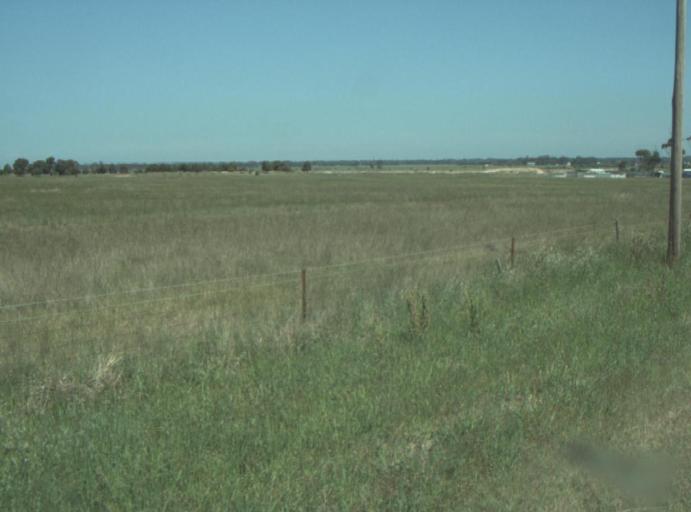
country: AU
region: Victoria
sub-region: Greater Geelong
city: Lara
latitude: -37.9689
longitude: 144.4060
